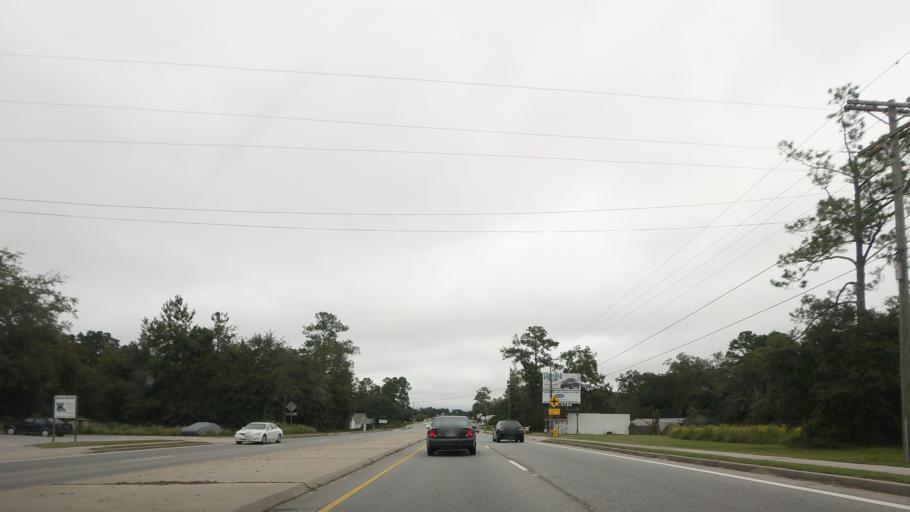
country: US
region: Georgia
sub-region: Lowndes County
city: Valdosta
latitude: 30.9313
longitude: -83.2435
